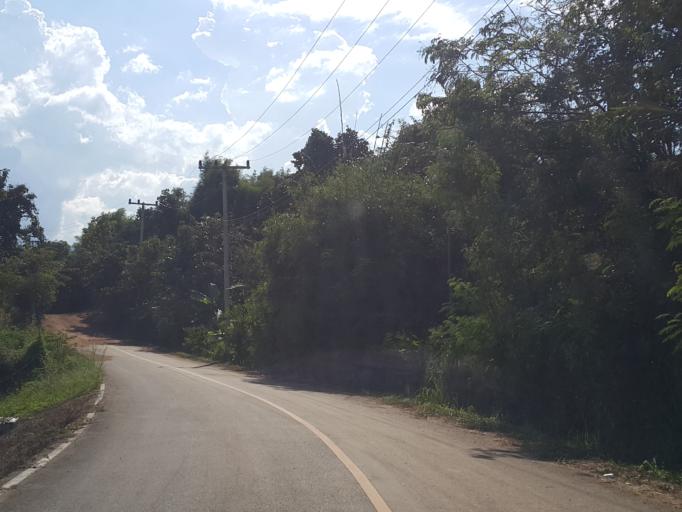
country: TH
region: Chiang Mai
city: San Sai
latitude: 18.9474
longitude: 98.9141
